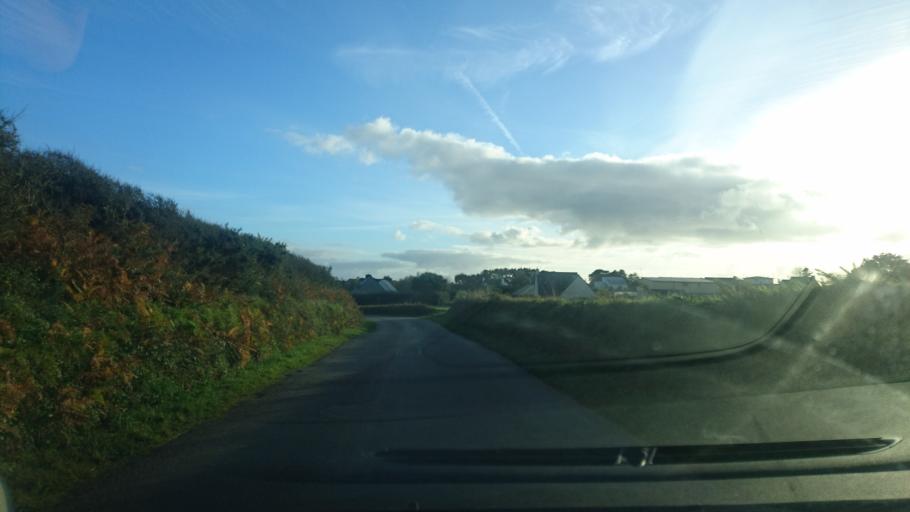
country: FR
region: Brittany
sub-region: Departement du Finistere
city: Lampaul-Plouarzel
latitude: 48.4279
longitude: -4.7693
